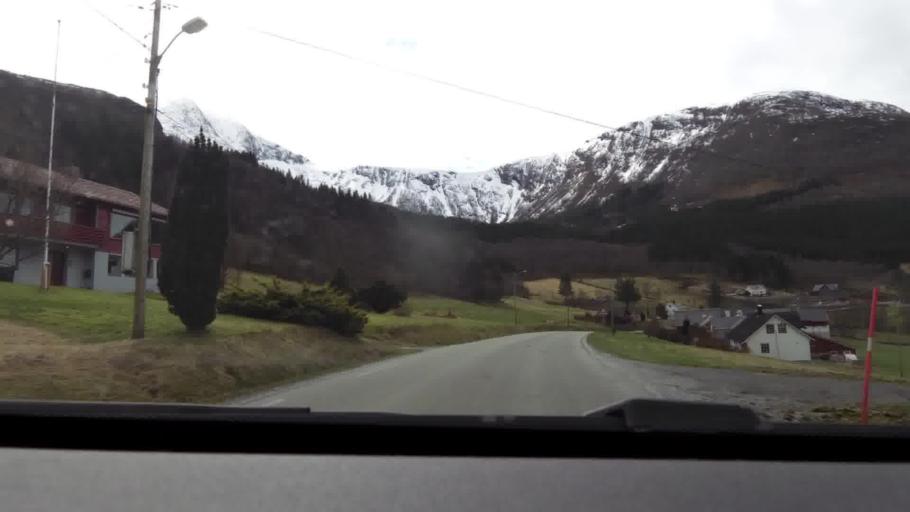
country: NO
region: More og Romsdal
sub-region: Gjemnes
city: Batnfjordsora
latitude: 62.9271
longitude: 7.5974
